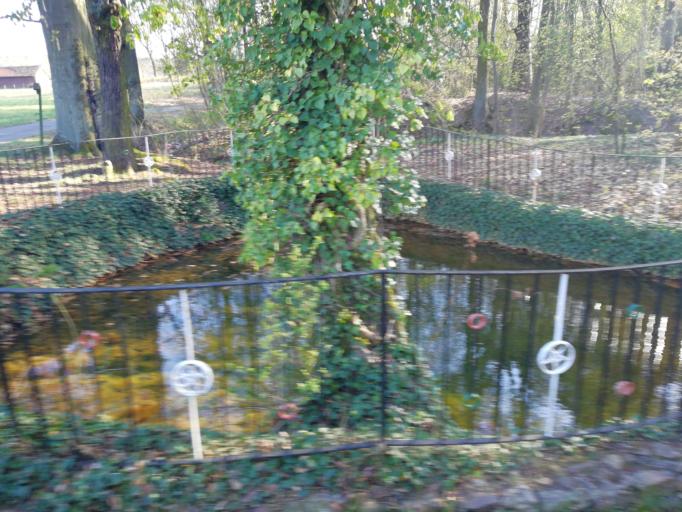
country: DE
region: Brandenburg
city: Calau
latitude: 51.7210
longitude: 13.9543
